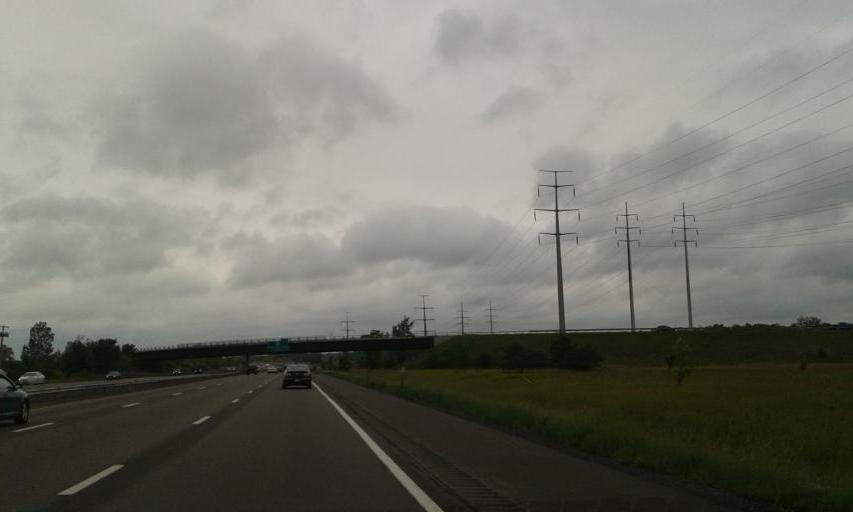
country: US
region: New York
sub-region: Erie County
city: Amherst
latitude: 42.9960
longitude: -78.8053
